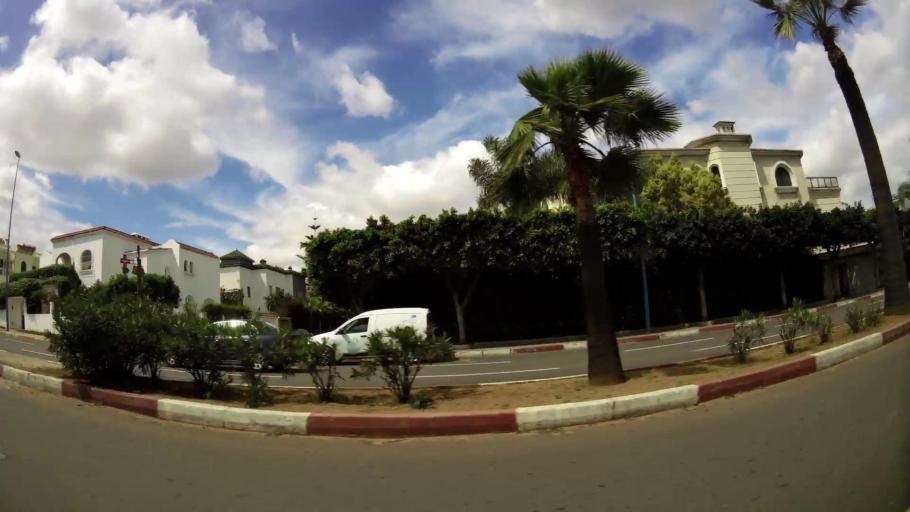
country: MA
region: Grand Casablanca
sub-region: Casablanca
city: Casablanca
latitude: 33.5515
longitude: -7.6231
